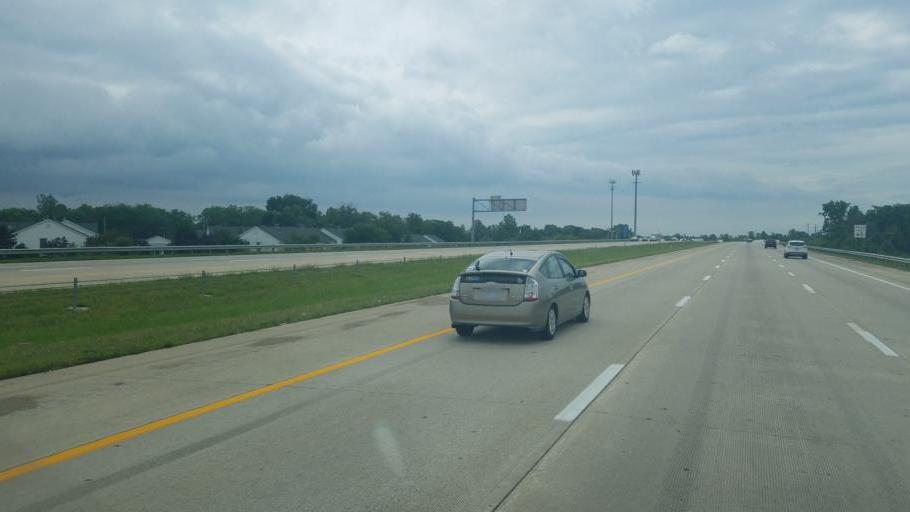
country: US
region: Ohio
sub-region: Franklin County
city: Grove City
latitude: 39.9156
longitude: -83.1112
